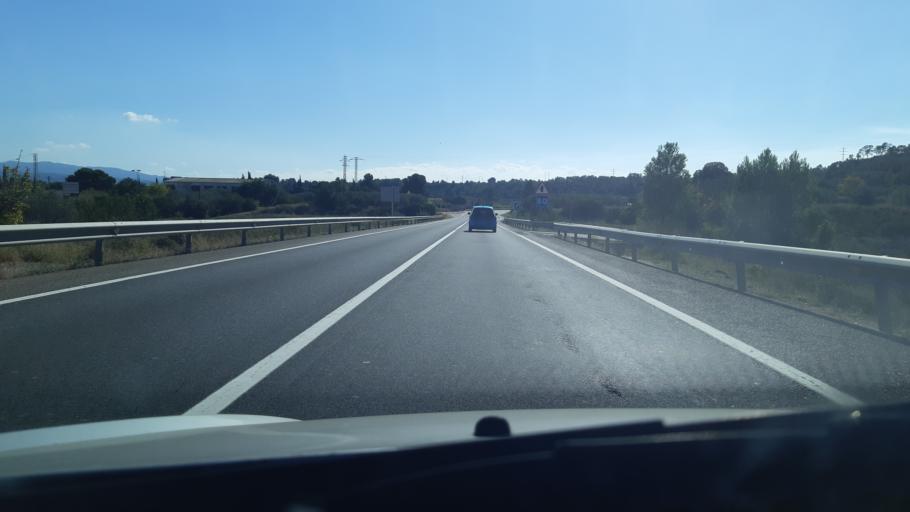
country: ES
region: Catalonia
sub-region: Provincia de Tarragona
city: Tivenys
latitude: 40.9071
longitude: 0.4832
